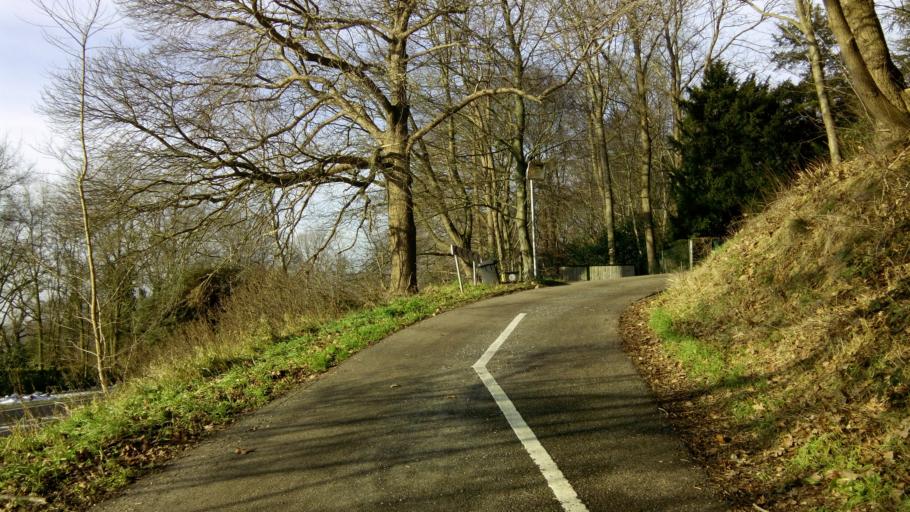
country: NL
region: Gelderland
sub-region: Gemeente Groesbeek
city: Bredeweg
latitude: 51.7383
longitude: 5.9178
